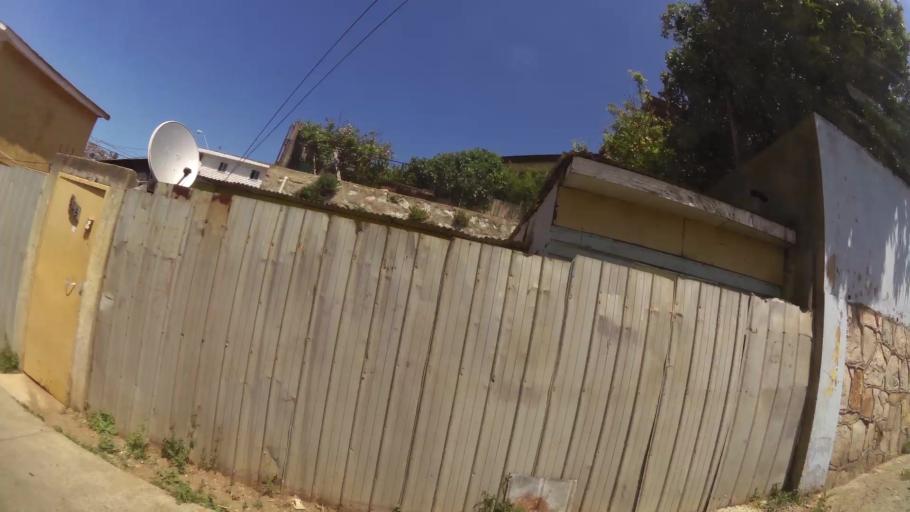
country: CL
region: Valparaiso
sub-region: Provincia de Valparaiso
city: Valparaiso
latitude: -33.0390
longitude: -71.6391
